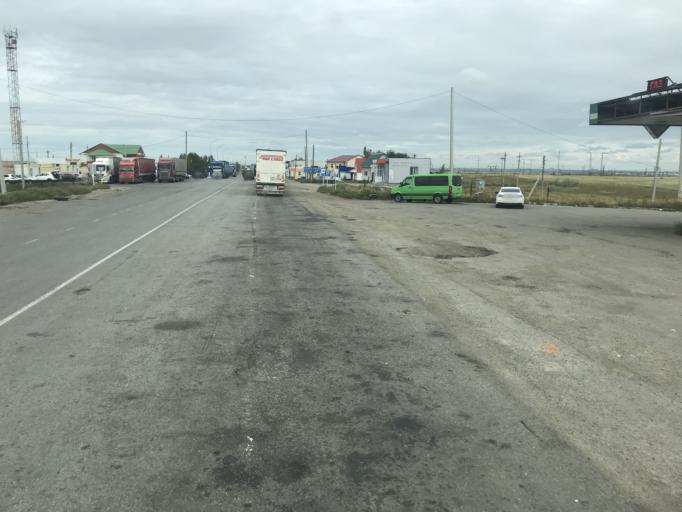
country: RU
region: Chelyabinsk
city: Bobrovka
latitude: 53.9977
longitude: 61.6435
